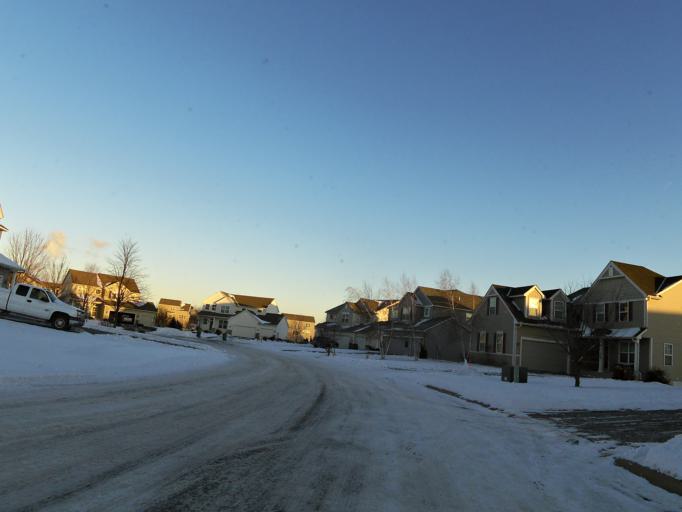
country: US
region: Minnesota
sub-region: Dakota County
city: Rosemount
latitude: 44.7419
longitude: -93.0993
